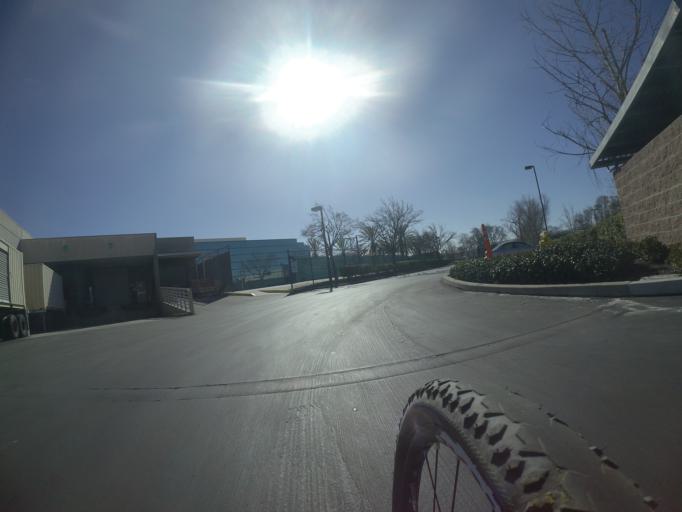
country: US
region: California
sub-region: Santa Clara County
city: Milpitas
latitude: 37.4738
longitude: -121.9335
